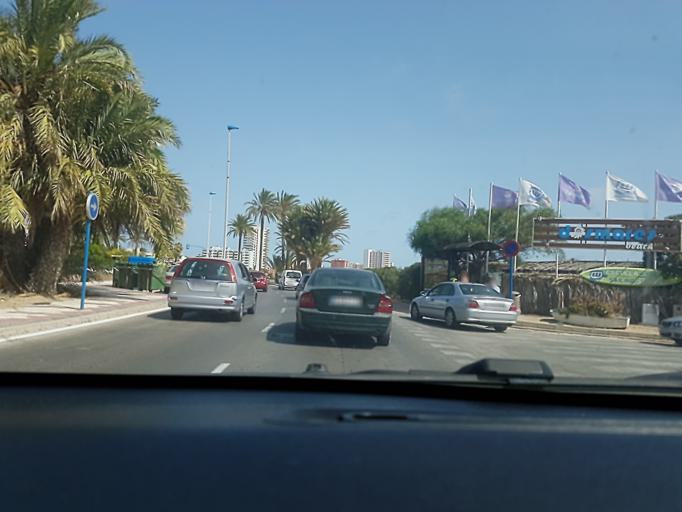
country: ES
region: Murcia
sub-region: Murcia
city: La Manga del Mar Menor
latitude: 37.6617
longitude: -0.7287
